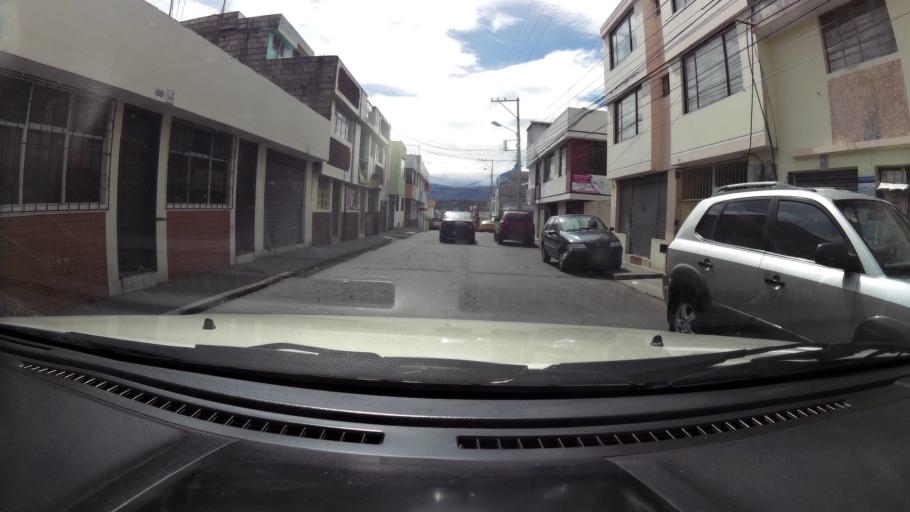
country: EC
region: Cotopaxi
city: Latacunga
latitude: -0.9270
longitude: -78.6195
